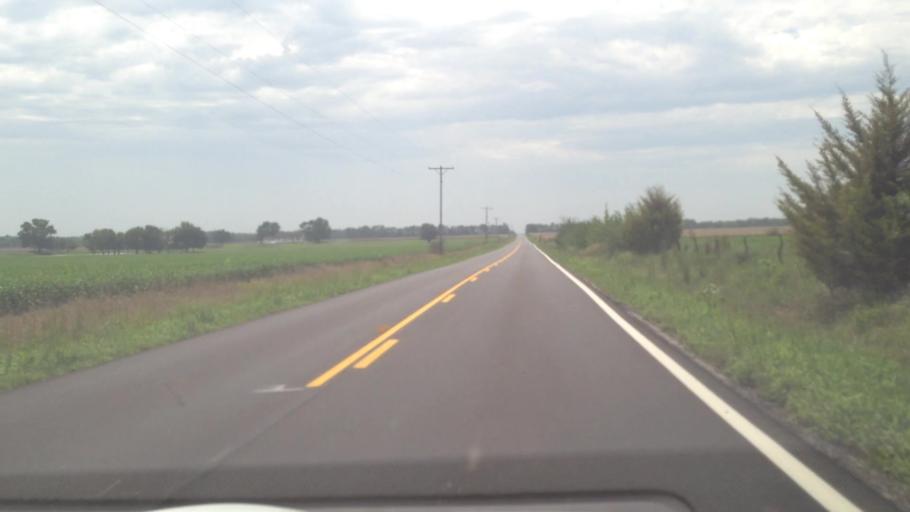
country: US
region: Kansas
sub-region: Crawford County
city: Girard
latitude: 37.6478
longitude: -94.9698
